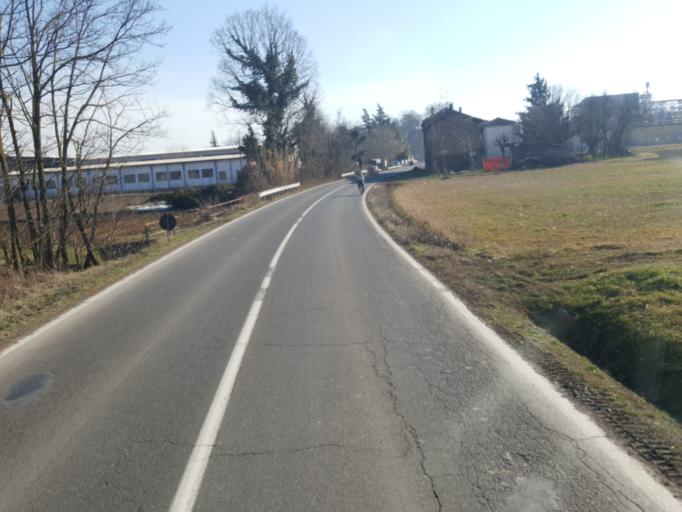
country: IT
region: Piedmont
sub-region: Provincia di Alessandria
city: Castellar Guidobono
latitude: 44.9061
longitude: 8.9382
